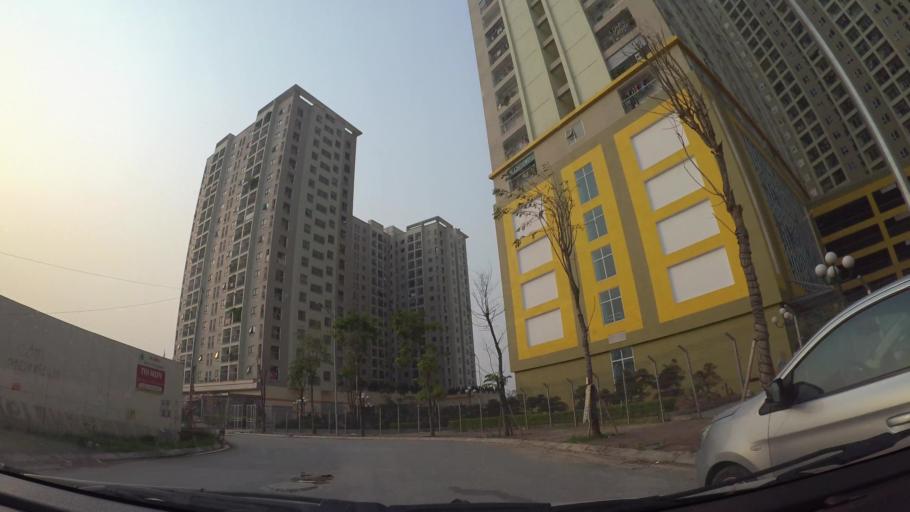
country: VN
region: Ha Noi
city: Cau Dien
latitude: 21.0053
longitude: 105.7272
